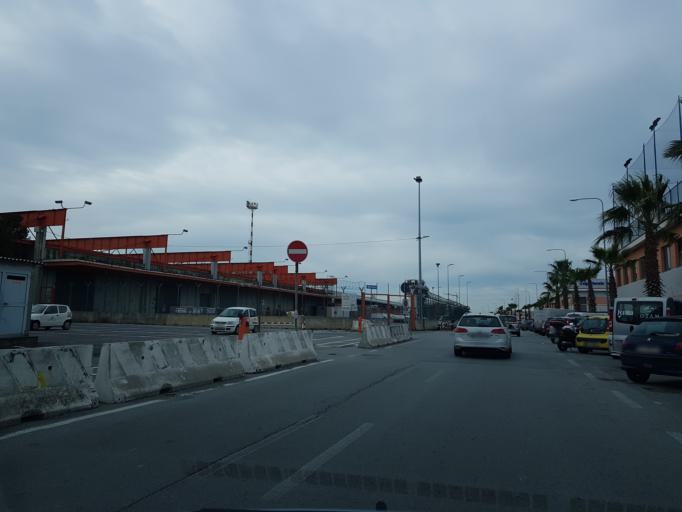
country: IT
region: Liguria
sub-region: Provincia di Genova
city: San Teodoro
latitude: 44.4168
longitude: 8.8464
